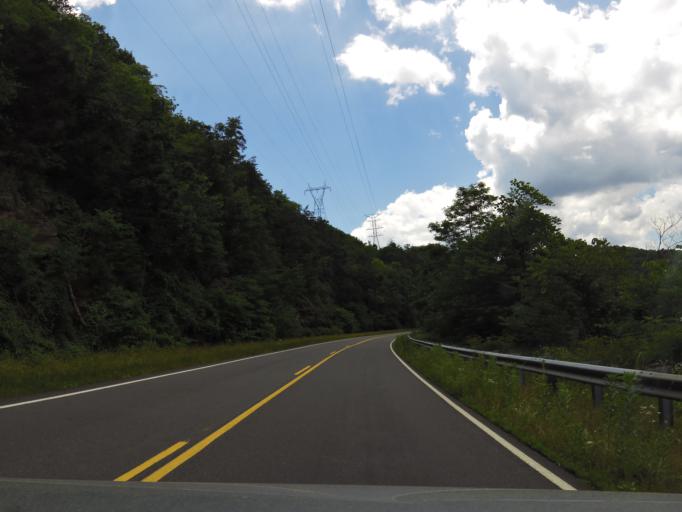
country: US
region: Tennessee
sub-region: Blount County
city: Maryville
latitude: 35.5492
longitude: -83.9918
